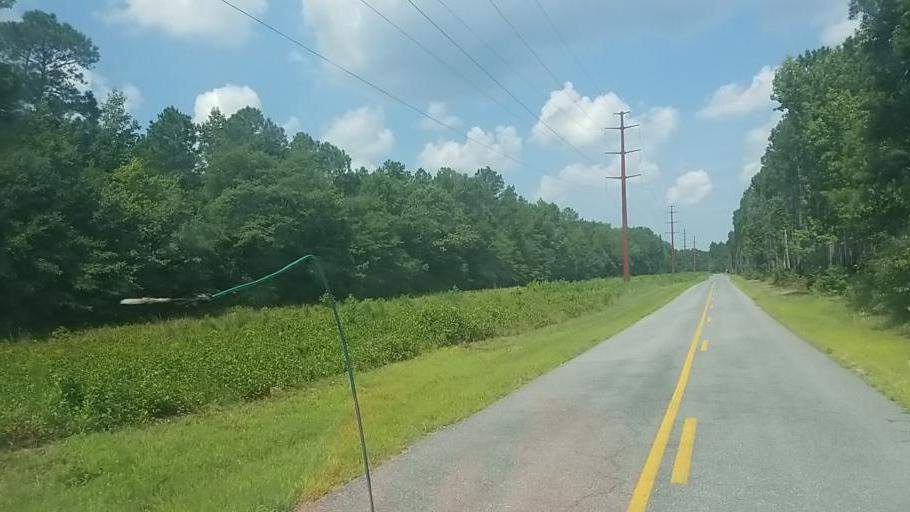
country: US
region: Maryland
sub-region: Worcester County
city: Snow Hill
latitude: 38.2641
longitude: -75.4661
